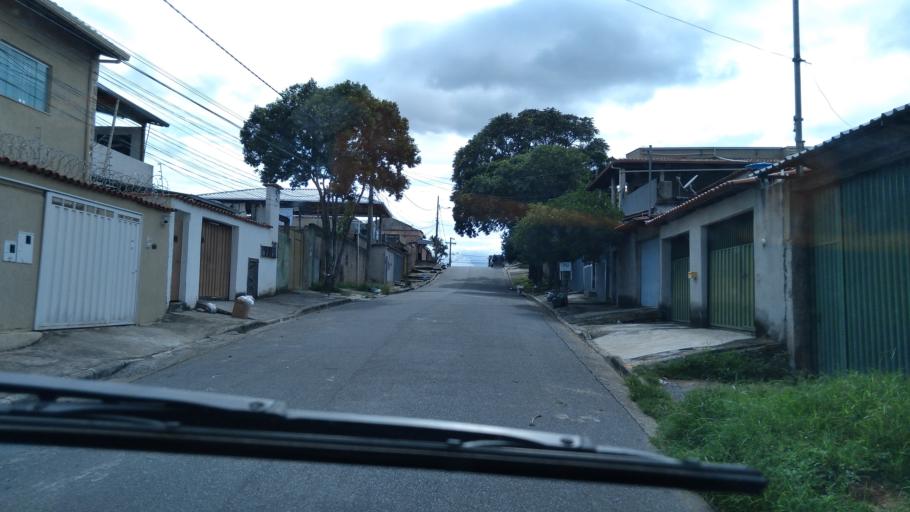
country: BR
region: Minas Gerais
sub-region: Santa Luzia
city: Santa Luzia
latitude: -19.8332
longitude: -43.8986
